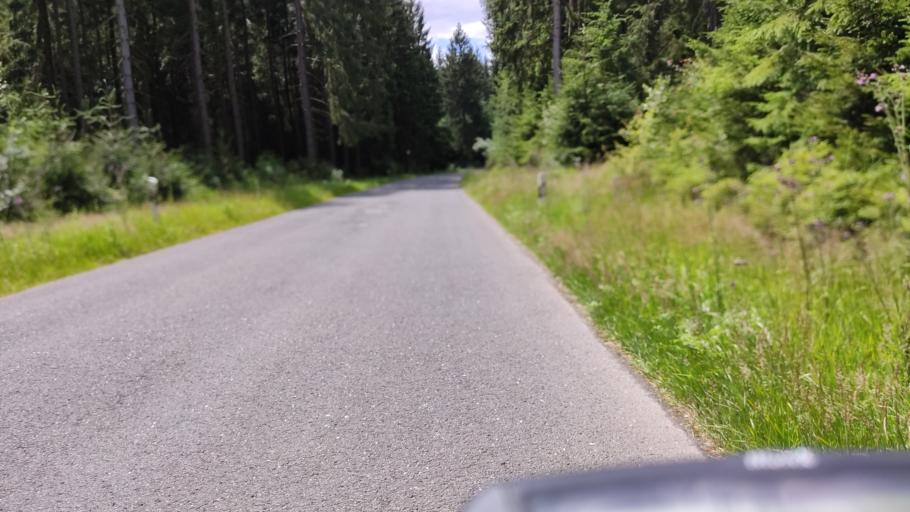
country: DE
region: Thuringia
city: Wurzbach
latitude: 50.4764
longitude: 11.4984
